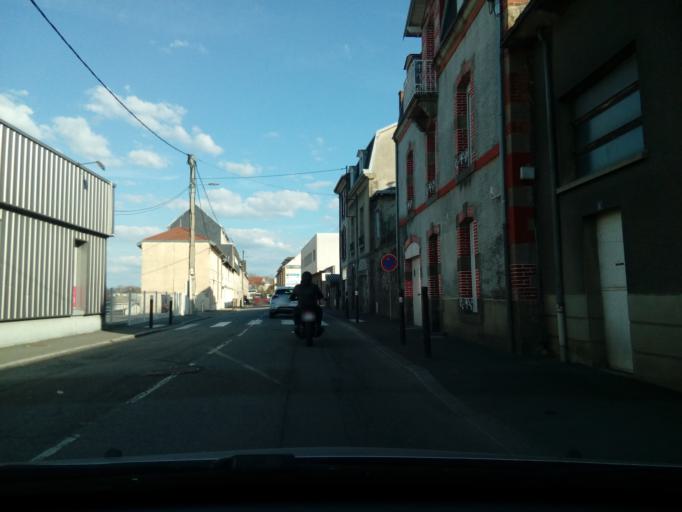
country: FR
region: Limousin
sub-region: Departement de la Creuse
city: Gueret
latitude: 46.1731
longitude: 1.8801
